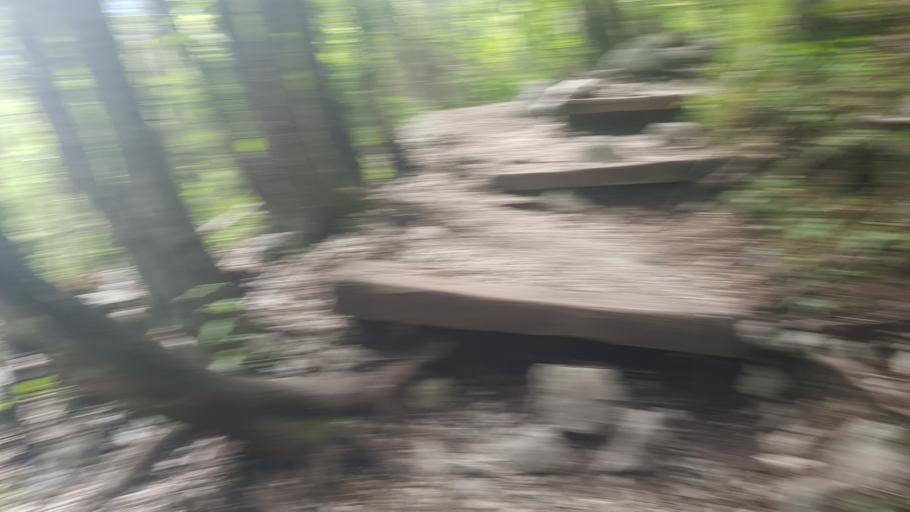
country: SI
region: Kranjska Gora
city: Kranjska Gora
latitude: 46.4108
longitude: 13.7246
